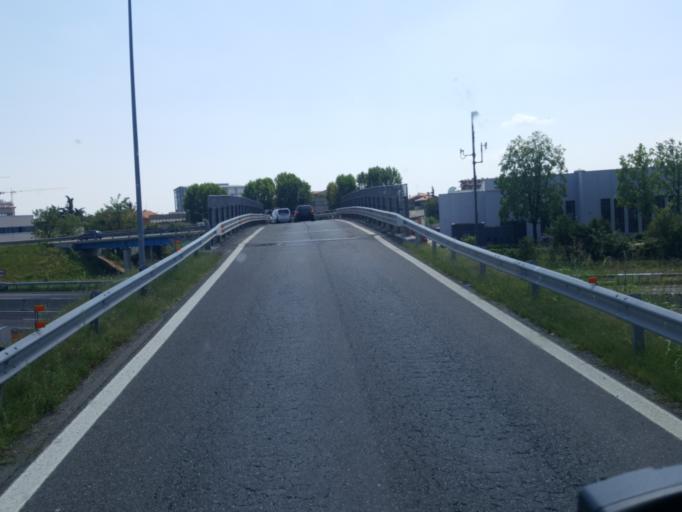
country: IT
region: Lombardy
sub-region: Citta metropolitana di Milano
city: Sesto San Giovanni
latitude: 45.5532
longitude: 9.2451
